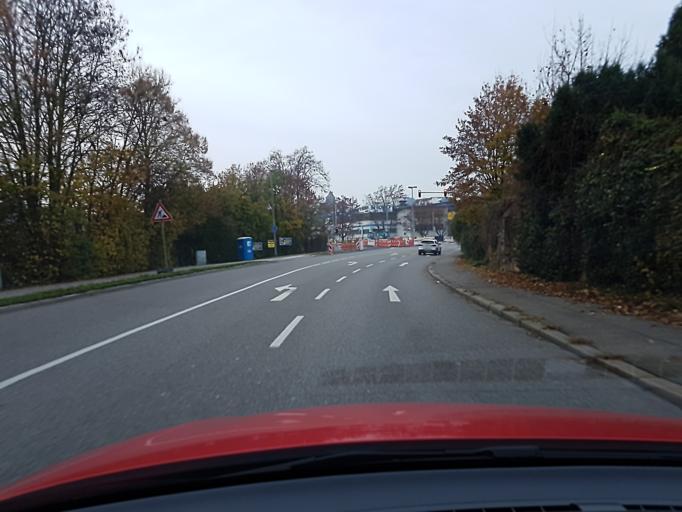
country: DE
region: Baden-Wuerttemberg
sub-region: Regierungsbezirk Stuttgart
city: Besigheim
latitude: 49.0041
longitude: 9.1449
